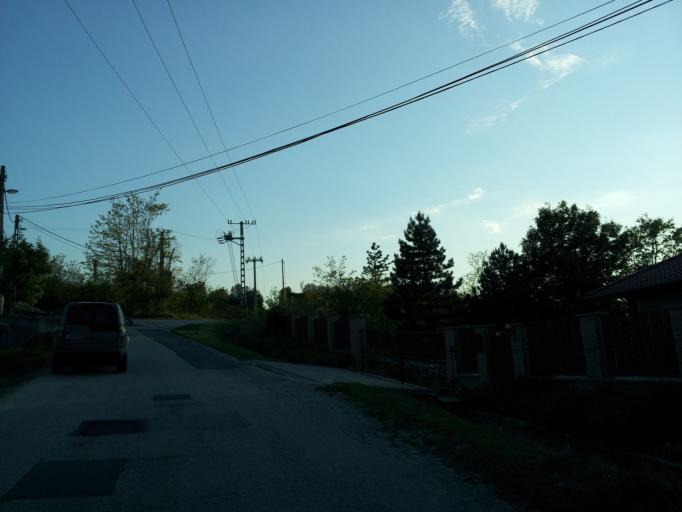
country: HU
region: Pest
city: Piliscsaba
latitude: 47.6278
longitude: 18.8117
